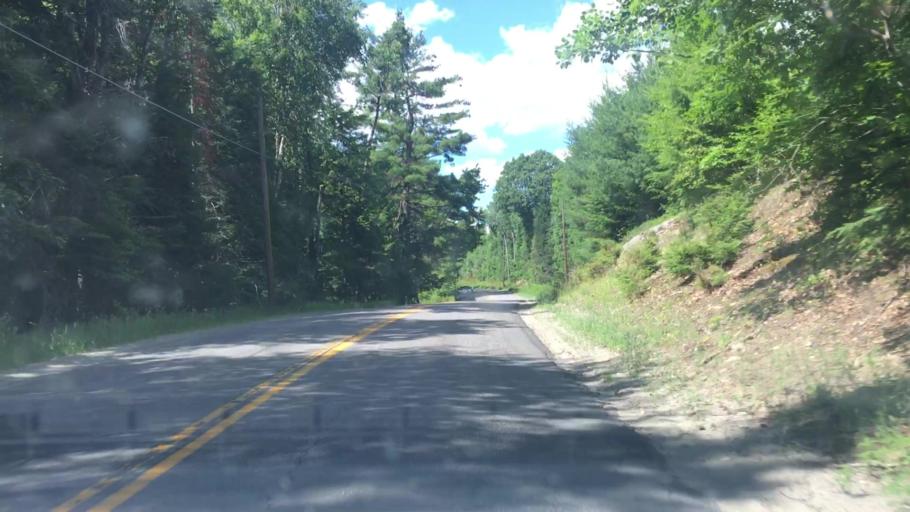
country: US
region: Maine
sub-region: Franklin County
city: Chesterville
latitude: 44.5736
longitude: -70.0896
